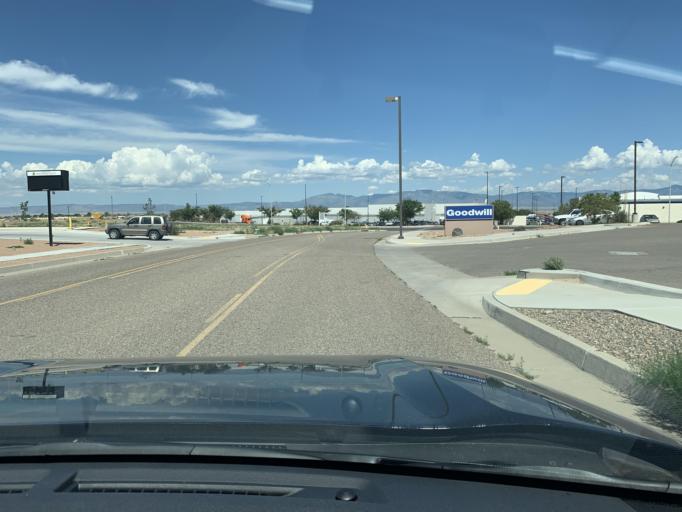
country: US
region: New Mexico
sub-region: Valencia County
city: Los Lunas
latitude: 34.8177
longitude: -106.7667
